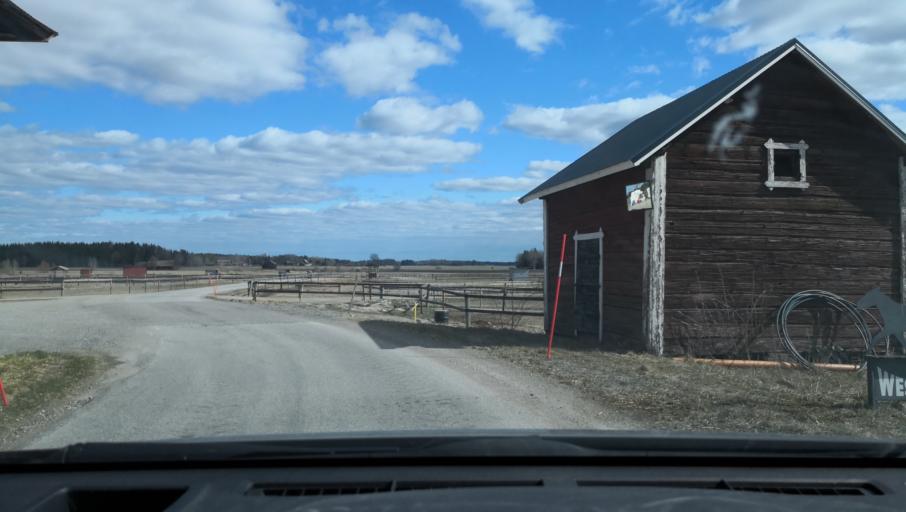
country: SE
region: Vaestmanland
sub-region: Sala Kommun
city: Sala
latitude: 59.8622
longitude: 16.5733
